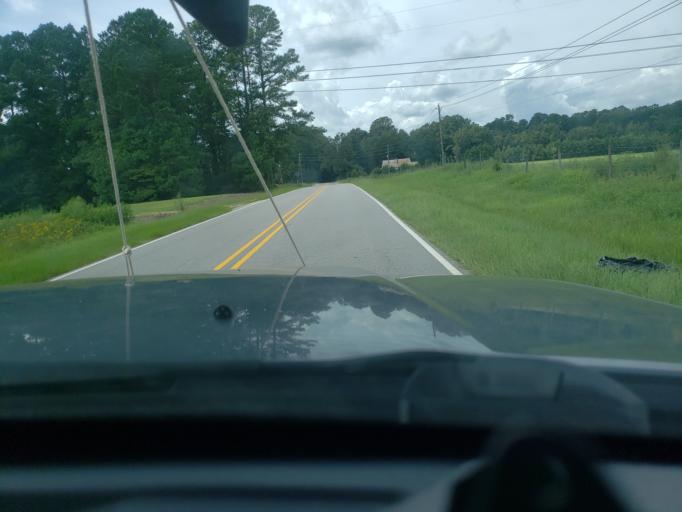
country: US
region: North Carolina
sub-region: Wake County
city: Rolesville
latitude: 35.8825
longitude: -78.4006
